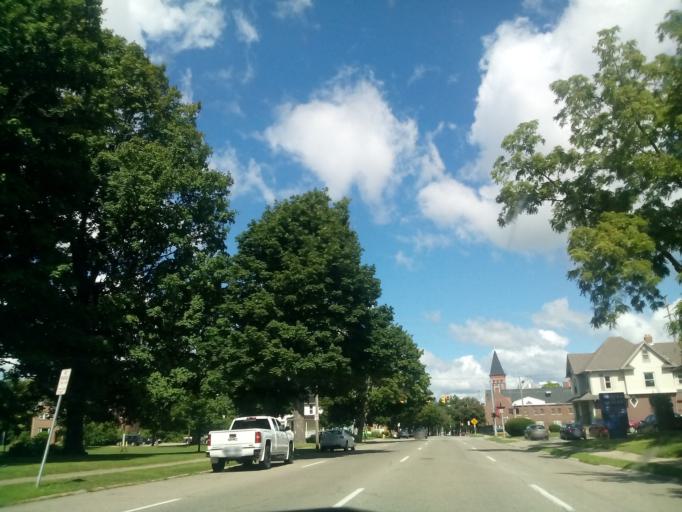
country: US
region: Michigan
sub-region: Genesee County
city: Flint
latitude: 43.0095
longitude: -83.6885
